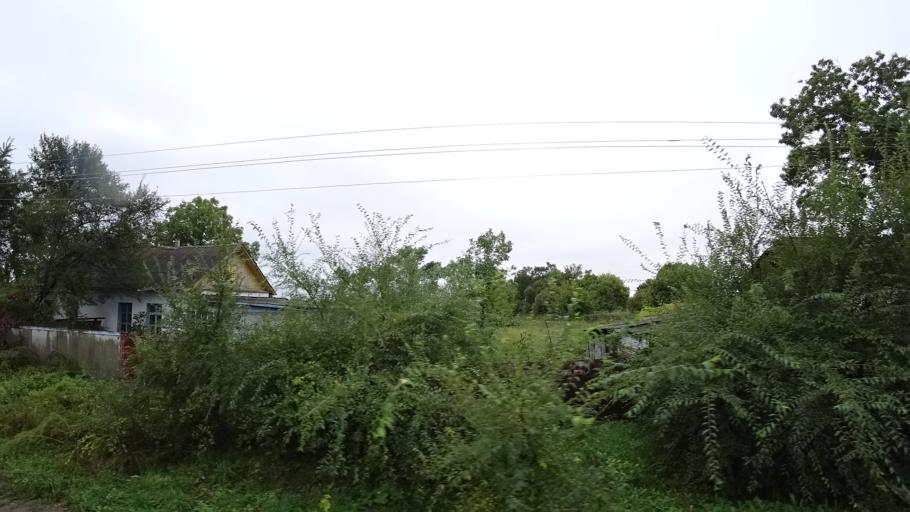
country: RU
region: Primorskiy
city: Monastyrishche
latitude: 44.2348
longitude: 132.4643
